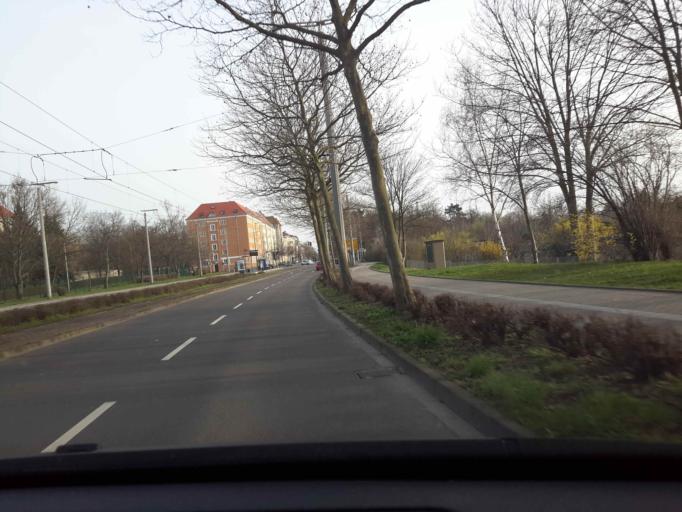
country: DE
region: Saxony
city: Leipzig
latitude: 51.3778
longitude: 12.3851
